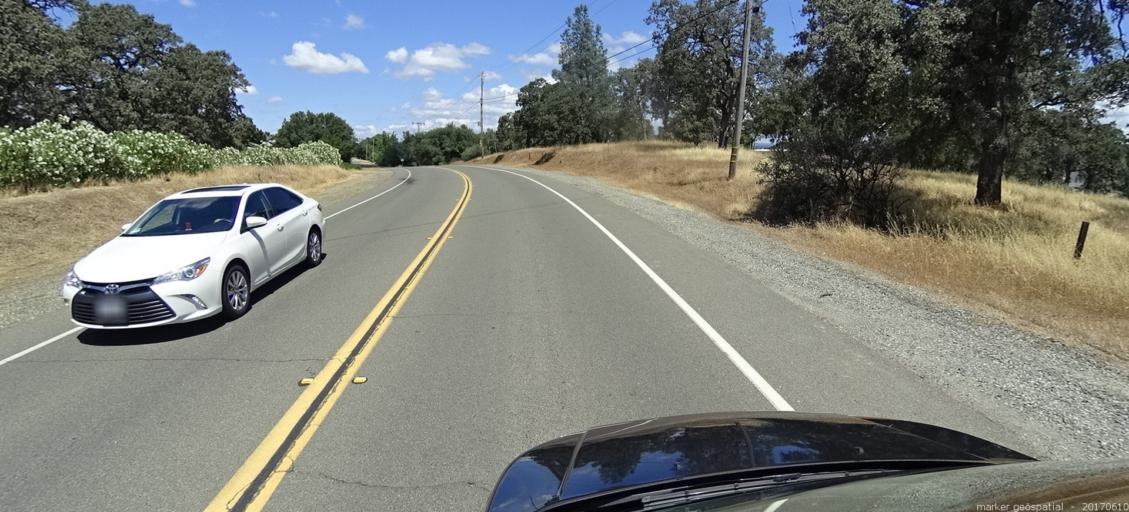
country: US
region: California
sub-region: Butte County
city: Oroville East
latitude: 39.5170
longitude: -121.4643
